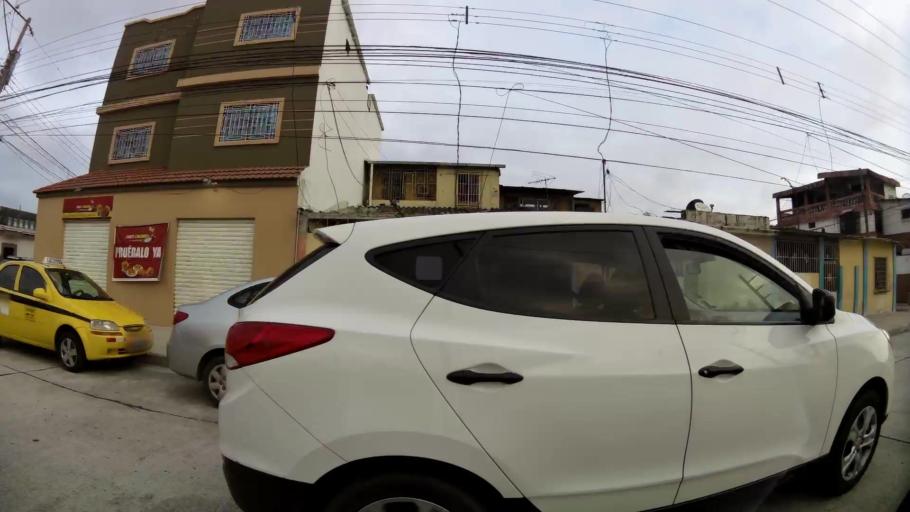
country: EC
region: Guayas
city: Eloy Alfaro
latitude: -2.1747
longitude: -79.8839
